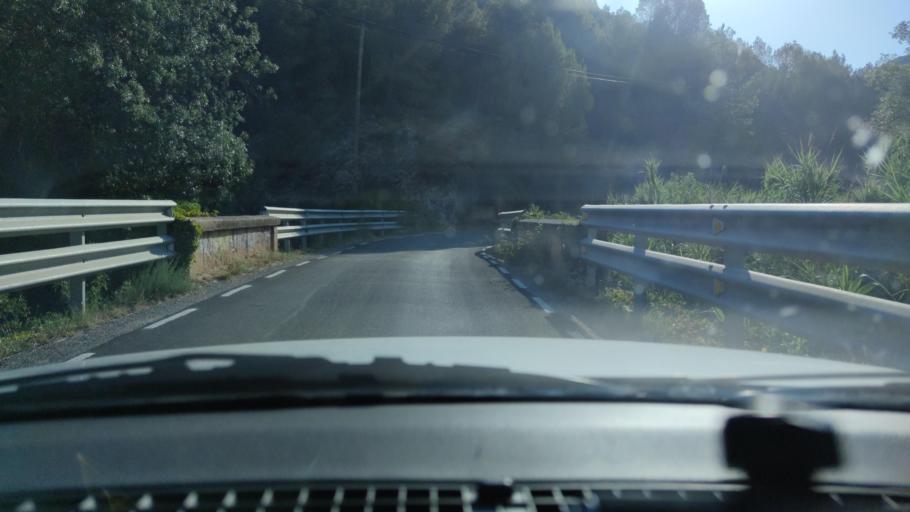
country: ES
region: Catalonia
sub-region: Provincia de Lleida
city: Camarasa
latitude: 41.8734
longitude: 0.8517
